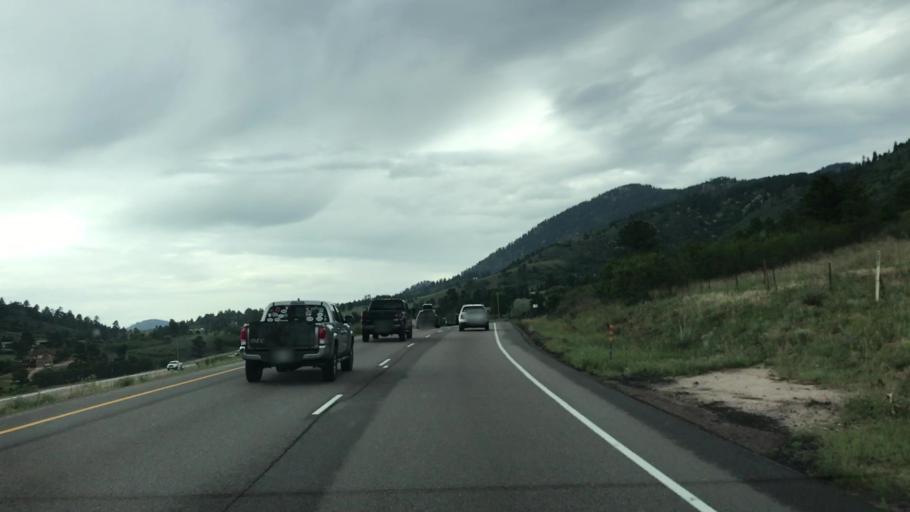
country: US
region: Colorado
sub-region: El Paso County
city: Cascade-Chipita Park
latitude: 38.9269
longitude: -104.9975
